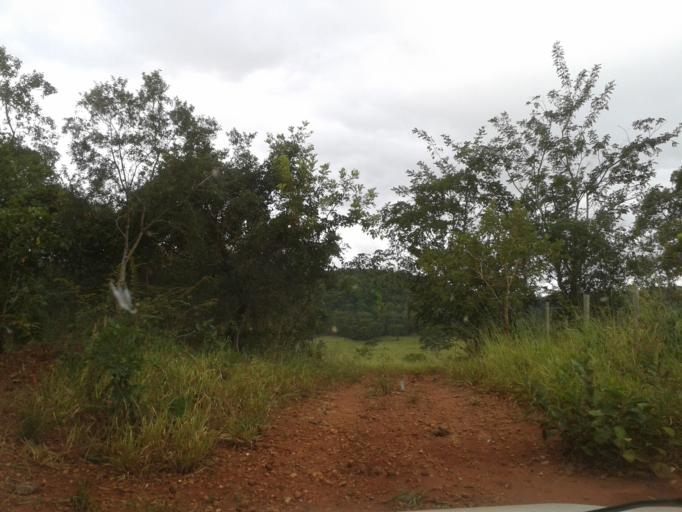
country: BR
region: Minas Gerais
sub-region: Campina Verde
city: Campina Verde
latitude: -19.4603
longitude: -49.5854
